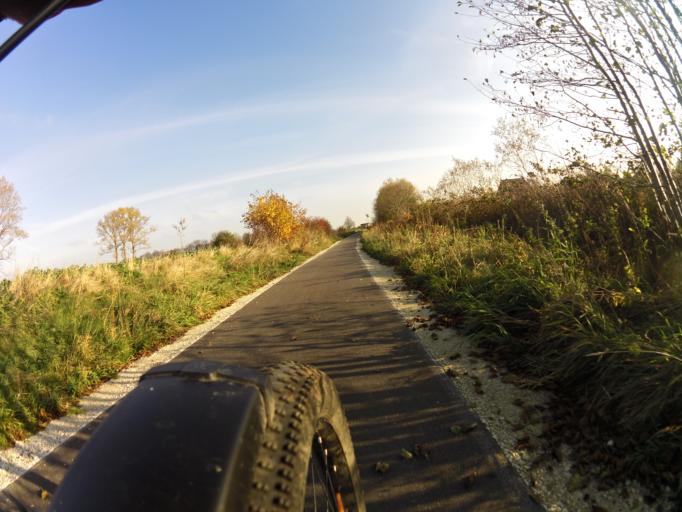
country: PL
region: Pomeranian Voivodeship
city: Strzelno
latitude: 54.7648
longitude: 18.2699
